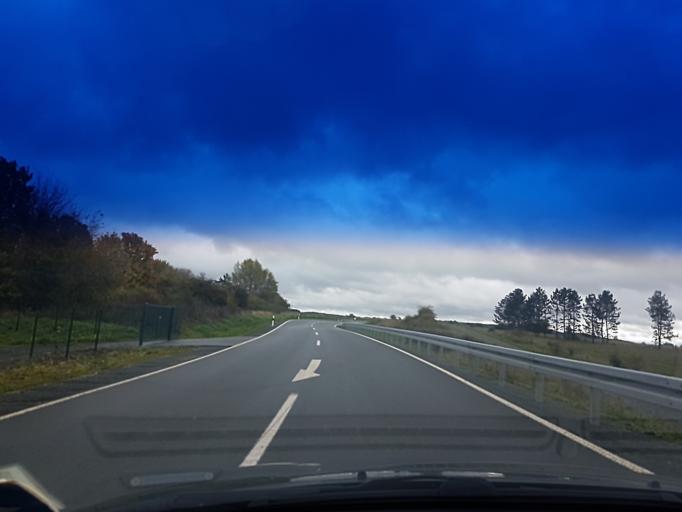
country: DE
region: Bavaria
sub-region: Upper Franconia
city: Bindlach
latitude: 49.9923
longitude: 11.6240
